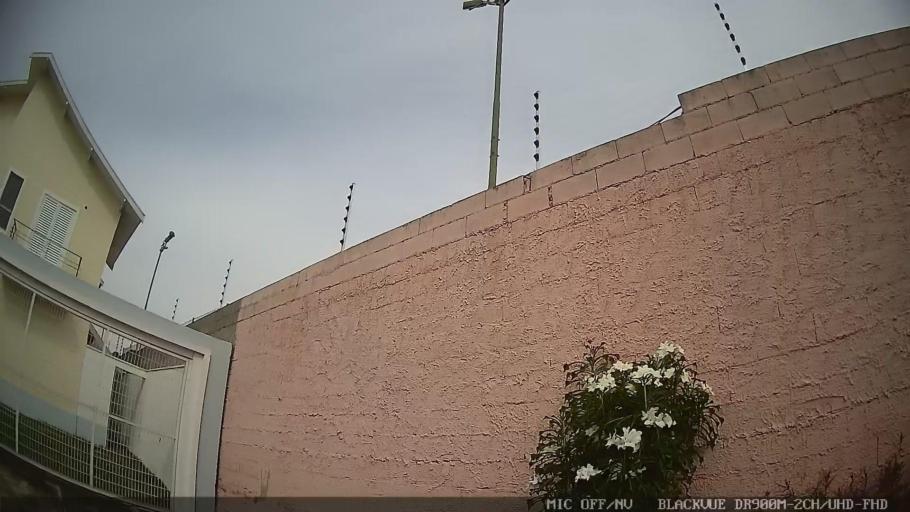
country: BR
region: Sao Paulo
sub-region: Indaiatuba
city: Indaiatuba
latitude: -23.0825
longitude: -47.2310
